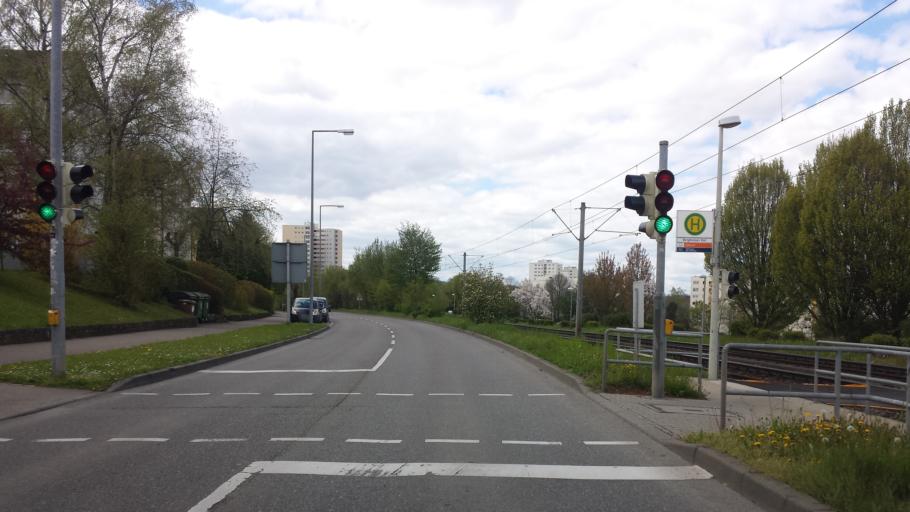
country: DE
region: Baden-Wuerttemberg
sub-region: Regierungsbezirk Stuttgart
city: Korntal
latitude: 48.8039
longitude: 9.1004
